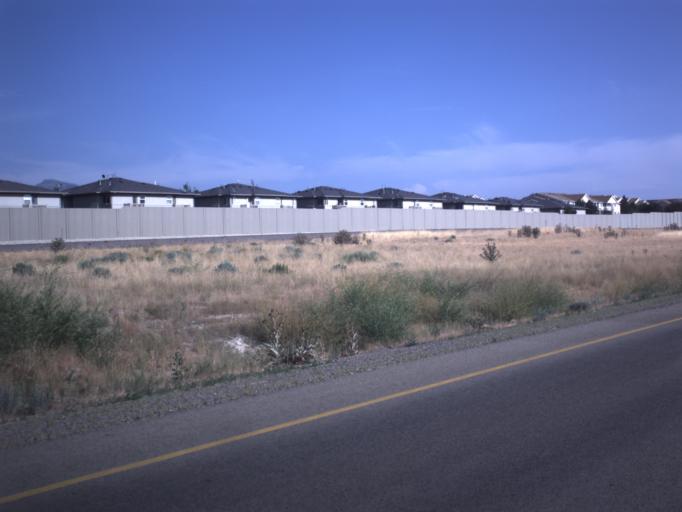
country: US
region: Utah
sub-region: Salt Lake County
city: Herriman
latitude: 40.5183
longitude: -112.0049
